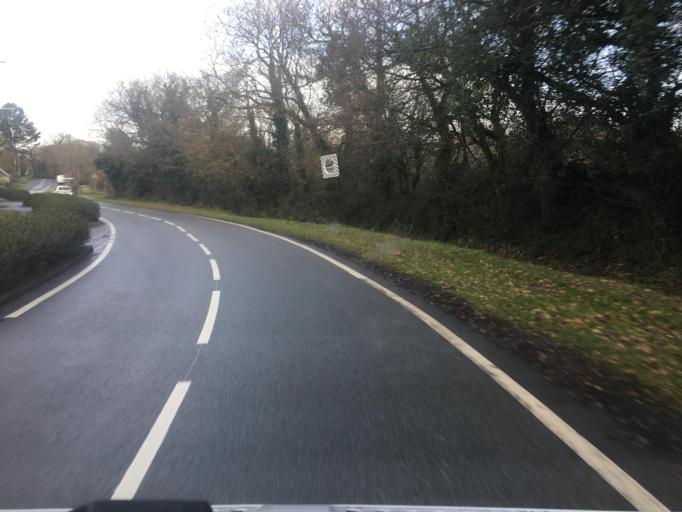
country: FR
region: Brittany
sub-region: Departement du Morbihan
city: Sarzeau
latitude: 47.5159
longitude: -2.7663
